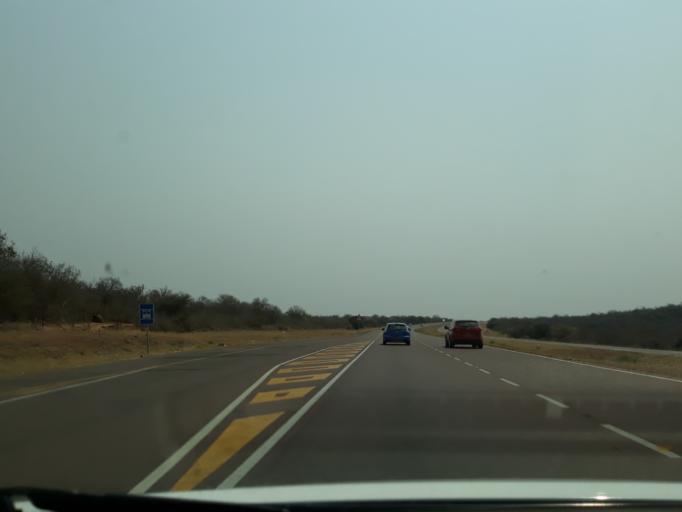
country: BW
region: Kgatleng
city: Bokaa
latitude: -24.4248
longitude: 26.0473
